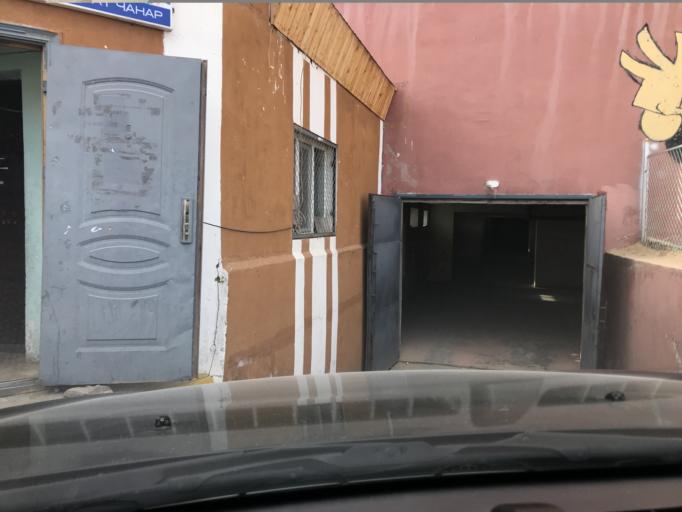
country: MN
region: Ulaanbaatar
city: Ulaanbaatar
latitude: 47.9164
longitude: 106.9523
